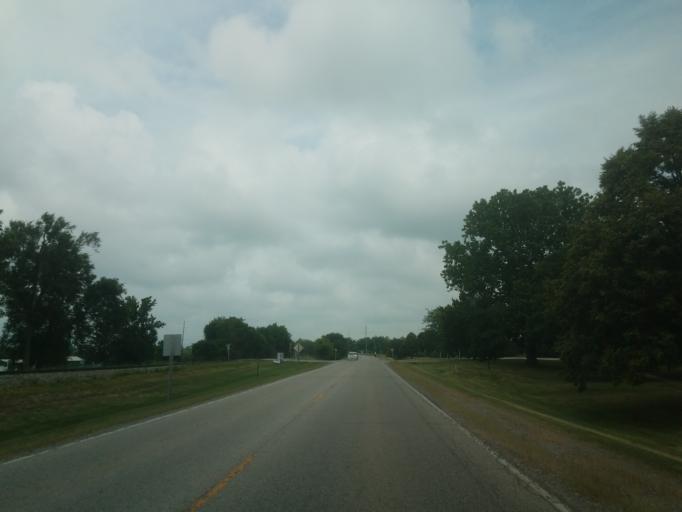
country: US
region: Illinois
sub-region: McLean County
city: Bloomington
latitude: 40.4857
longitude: -89.0149
